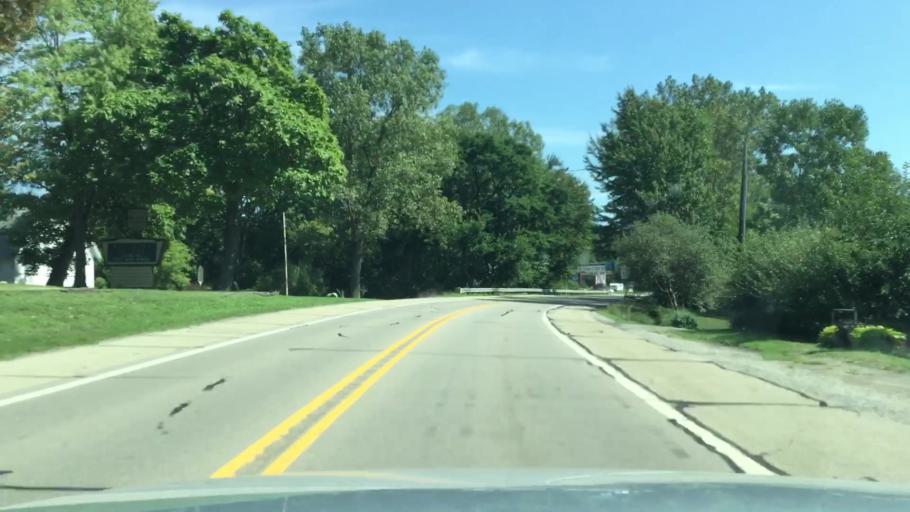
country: US
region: Michigan
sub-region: Washtenaw County
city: Manchester
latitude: 42.0625
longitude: -84.1176
